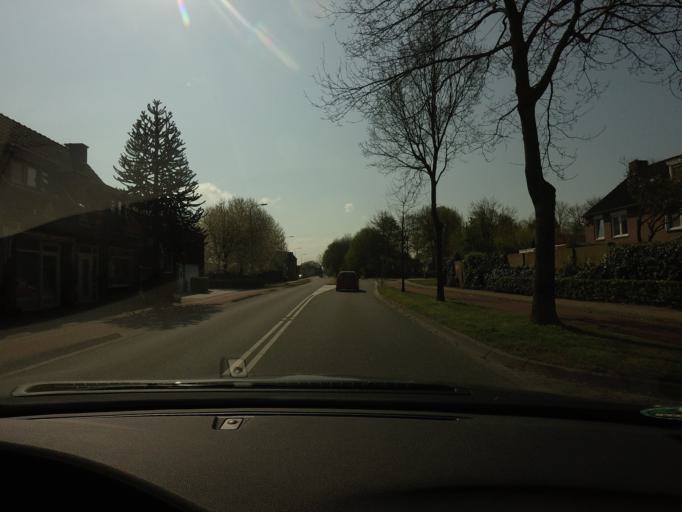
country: NL
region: Limburg
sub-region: Gemeente Maastricht
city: Heer
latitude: 50.8322
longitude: 5.7278
